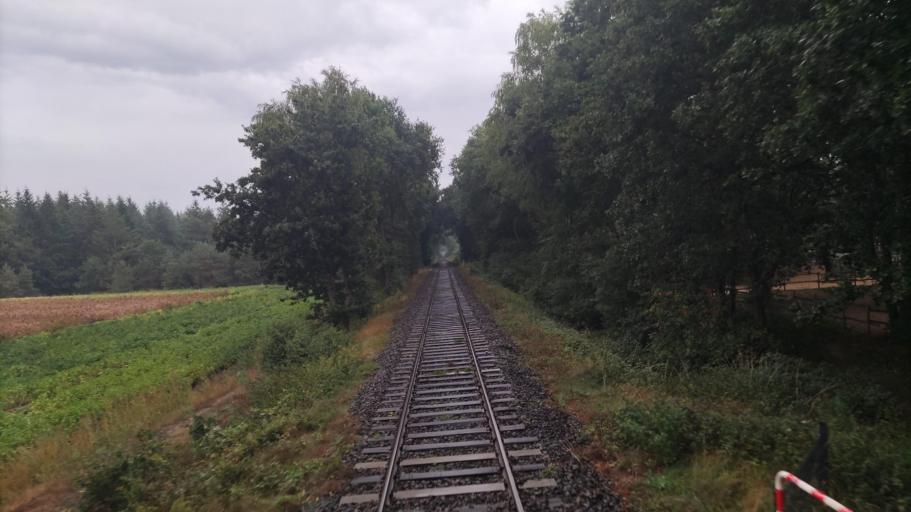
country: DE
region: Lower Saxony
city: Bispingen
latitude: 53.0945
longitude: 10.0104
